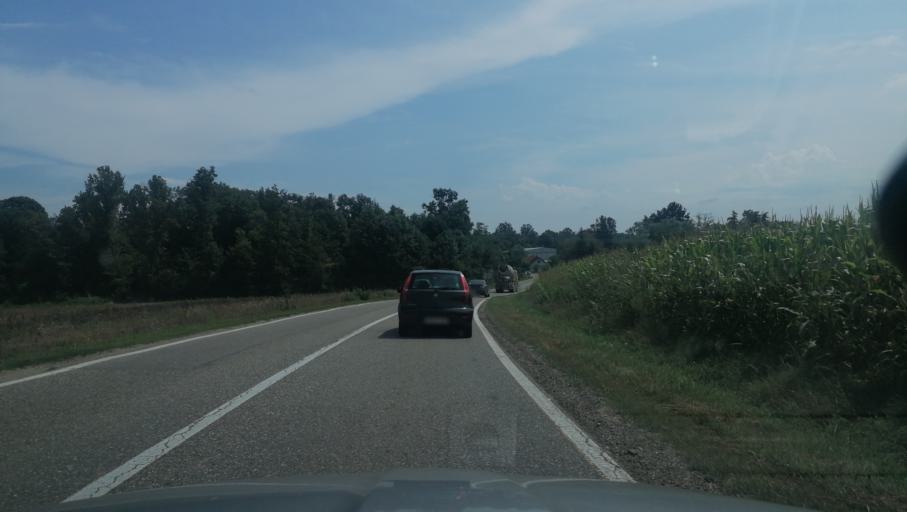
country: BA
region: Republika Srpska
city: Velika Obarska
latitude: 44.8143
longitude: 19.0584
